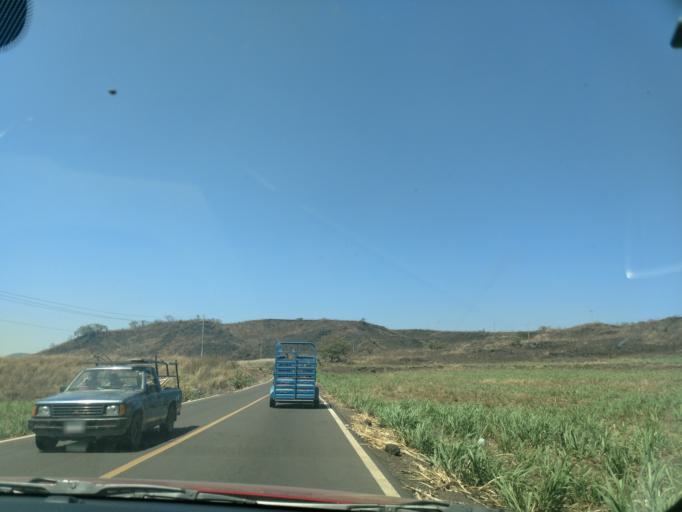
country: MX
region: Nayarit
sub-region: Tepic
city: La Corregidora
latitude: 21.5005
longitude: -104.7613
